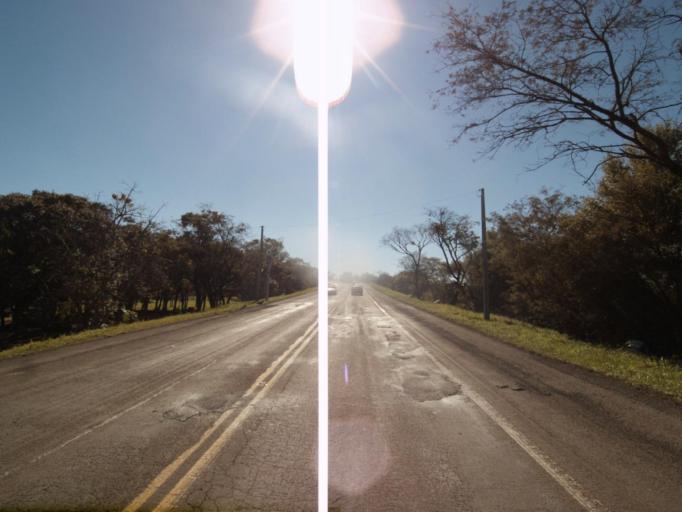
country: AR
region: Misiones
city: Bernardo de Irigoyen
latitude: -26.7882
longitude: -53.4580
